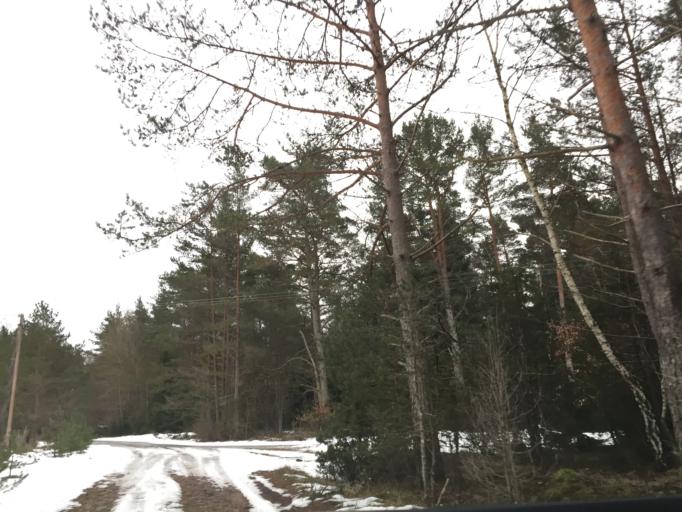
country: EE
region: Saare
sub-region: Kuressaare linn
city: Kuressaare
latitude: 58.4789
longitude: 22.2512
